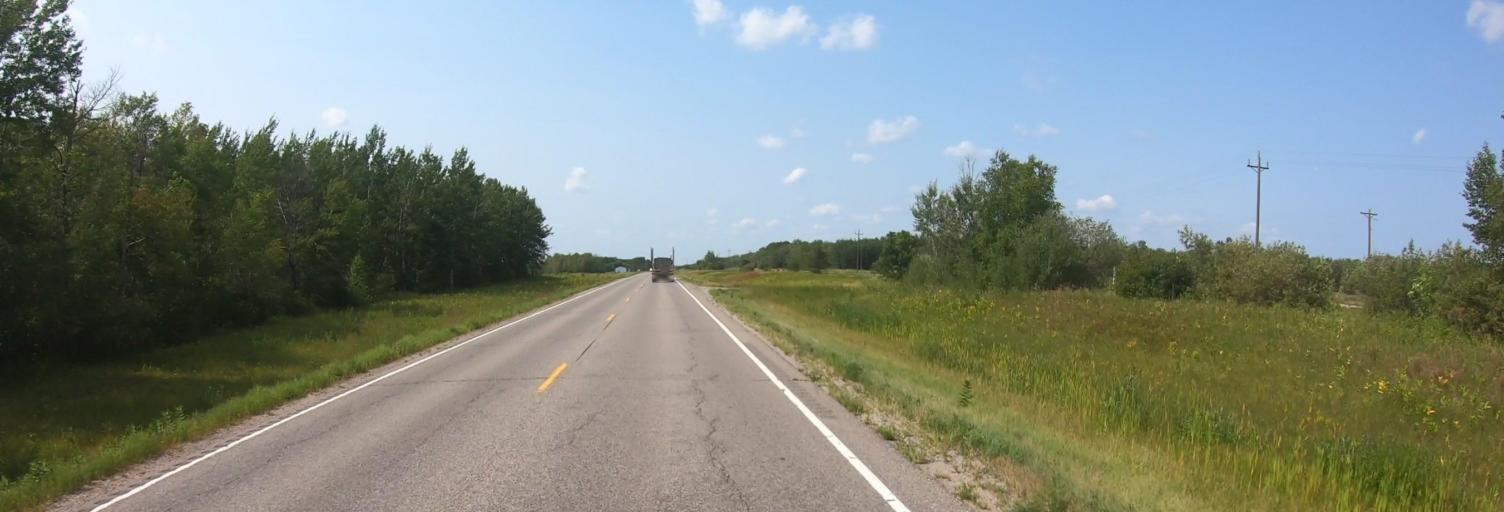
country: US
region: Minnesota
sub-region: Roseau County
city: Warroad
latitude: 48.8325
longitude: -95.1712
